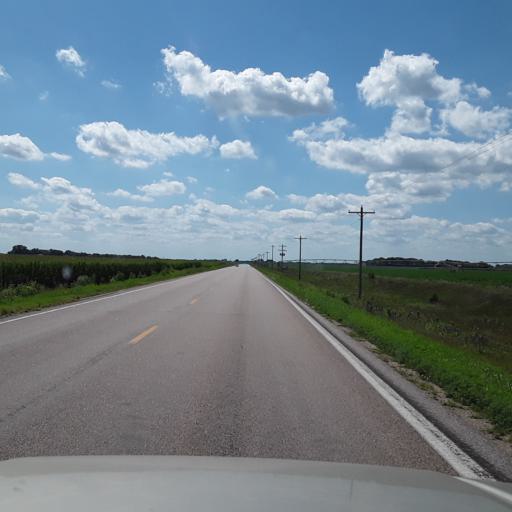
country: US
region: Nebraska
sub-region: Merrick County
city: Central City
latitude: 41.1911
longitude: -98.0409
